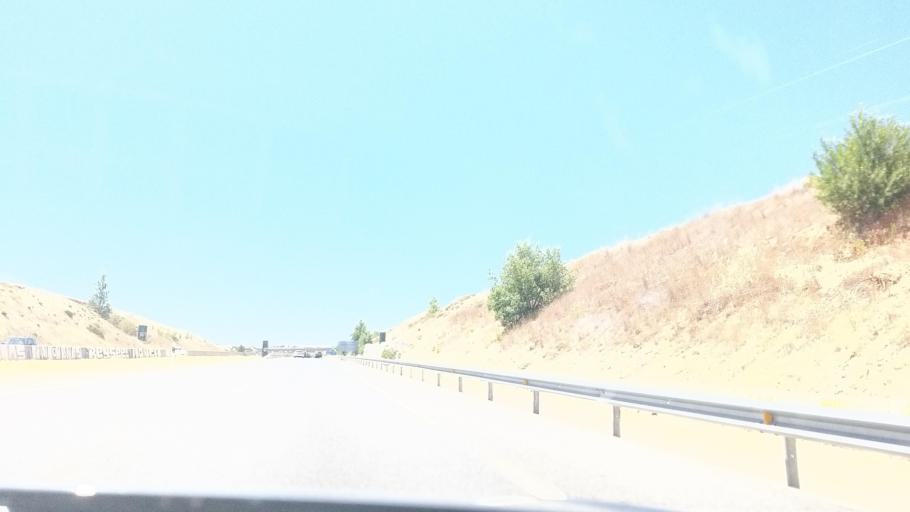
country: ES
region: Madrid
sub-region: Provincia de Madrid
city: El Molar
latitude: 40.7285
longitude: -3.5726
